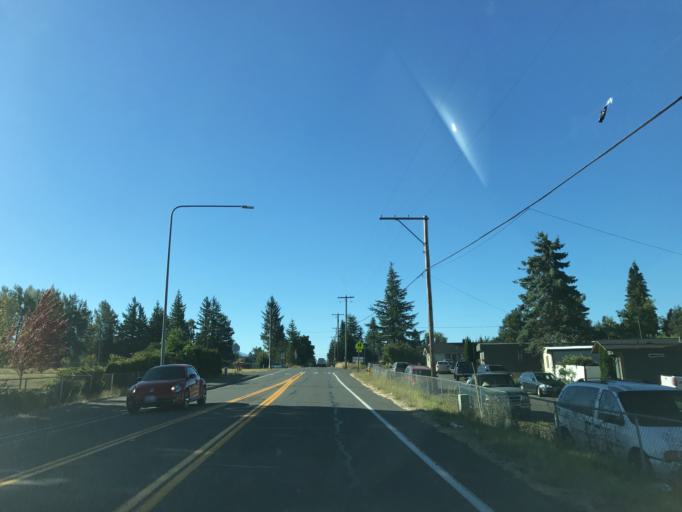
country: US
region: Washington
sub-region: King County
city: Enumclaw
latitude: 47.2220
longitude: -121.9898
